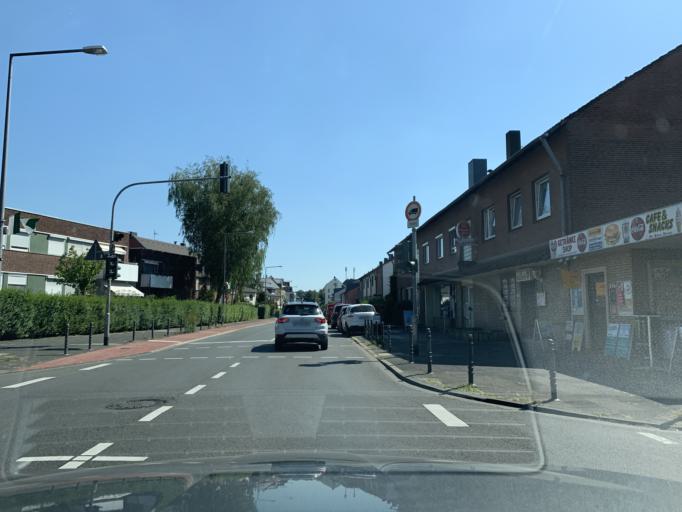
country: DE
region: North Rhine-Westphalia
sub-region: Regierungsbezirk Koln
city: Mengenich
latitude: 51.0014
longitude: 6.8773
